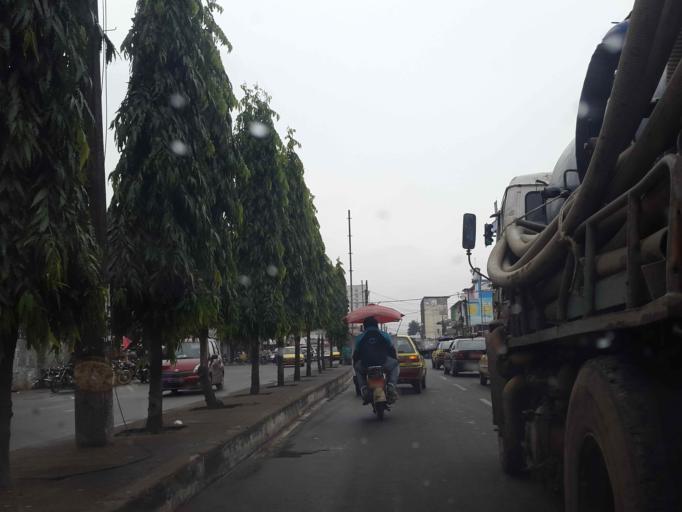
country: CM
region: Littoral
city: Douala
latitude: 4.0455
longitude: 9.6983
